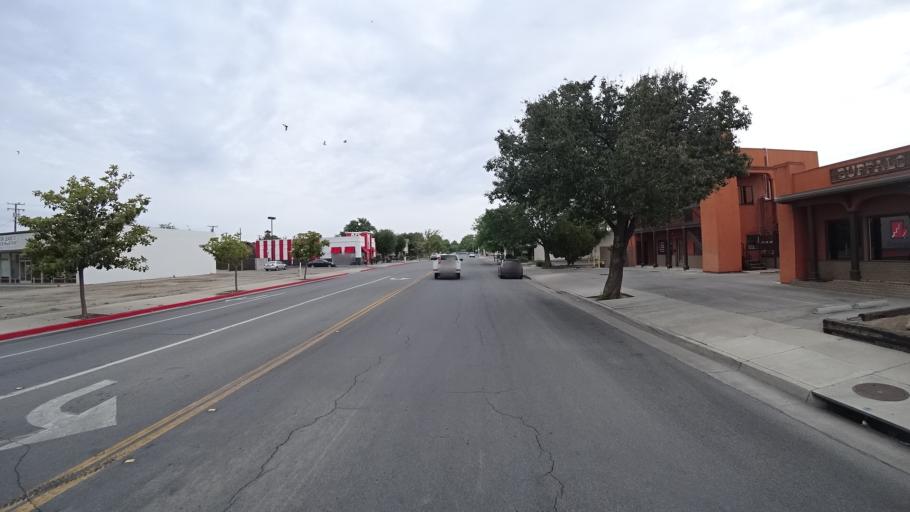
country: US
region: California
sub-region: Kings County
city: Hanford
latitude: 36.3281
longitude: -119.6493
